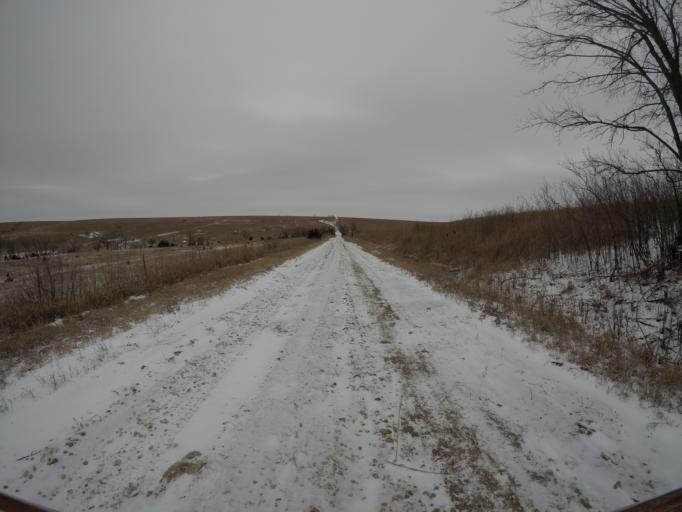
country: US
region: Kansas
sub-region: Wabaunsee County
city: Alma
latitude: 38.8850
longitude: -96.1136
